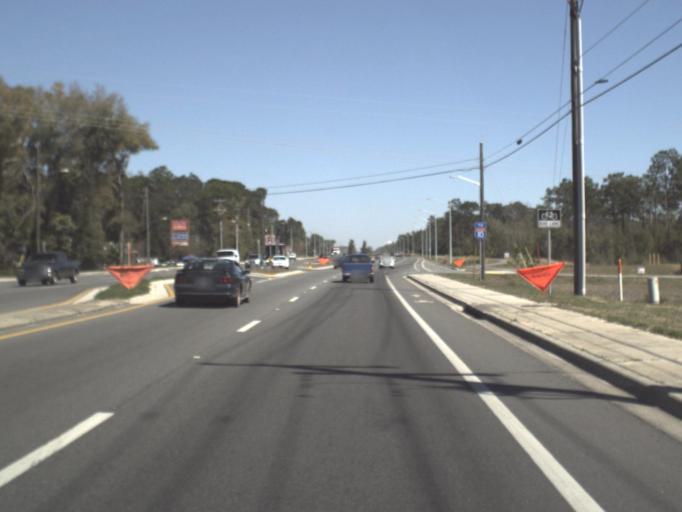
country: US
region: Florida
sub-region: Leon County
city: Tallahassee
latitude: 30.3758
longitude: -84.2909
